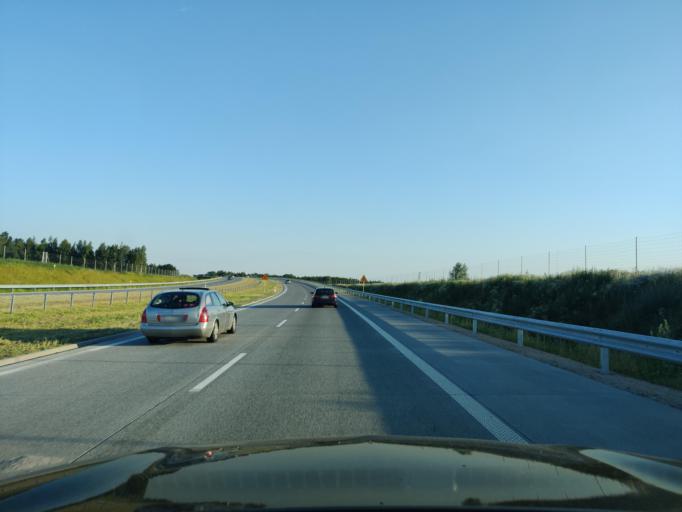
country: PL
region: Masovian Voivodeship
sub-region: Powiat mlawski
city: Wisniewo
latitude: 53.0155
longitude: 20.3375
